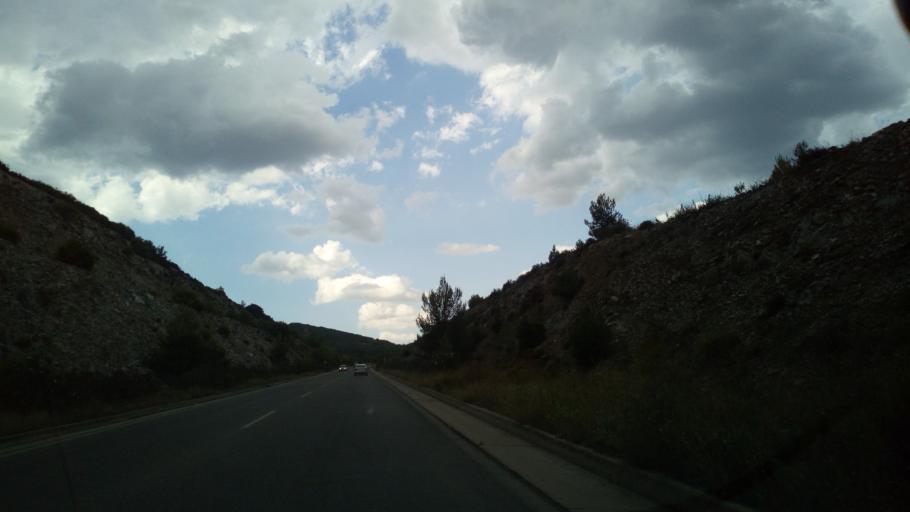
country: GR
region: Central Macedonia
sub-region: Nomos Chalkidikis
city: Polygyros
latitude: 40.3448
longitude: 23.4511
